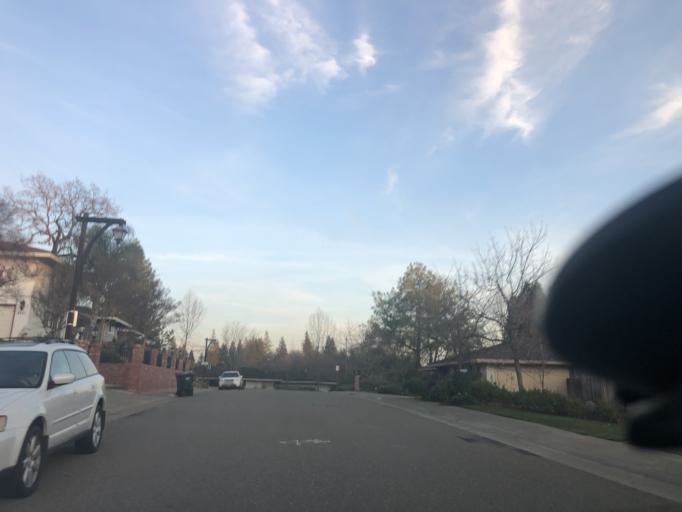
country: US
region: California
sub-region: Sacramento County
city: Gold River
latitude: 38.6413
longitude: -121.2274
